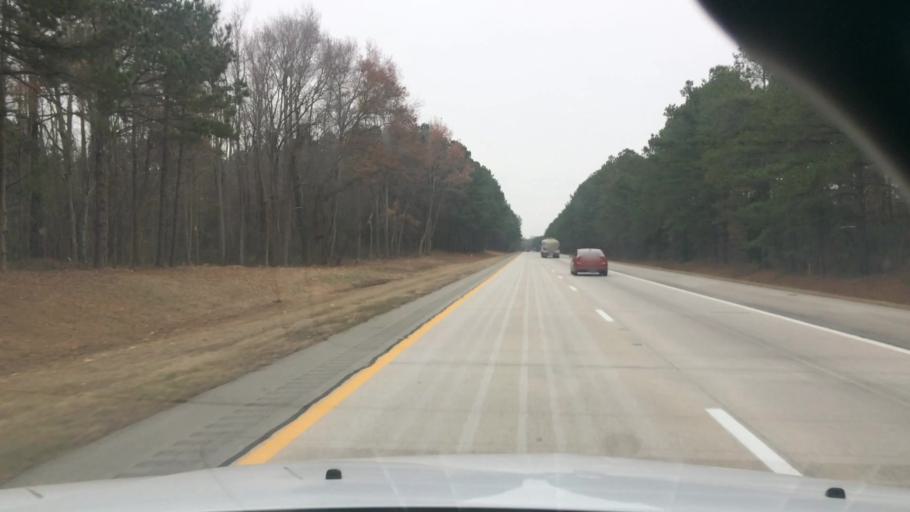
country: US
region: North Carolina
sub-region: Nash County
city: Nashville
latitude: 35.8845
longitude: -77.9436
